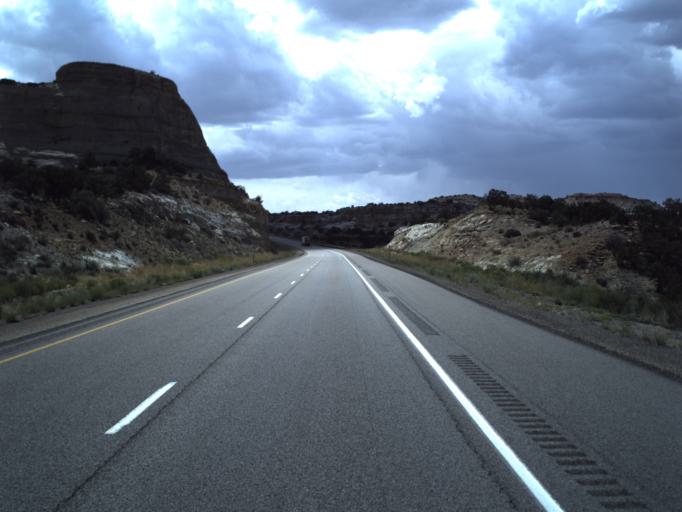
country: US
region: Utah
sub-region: Emery County
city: Ferron
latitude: 38.8552
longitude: -110.8750
